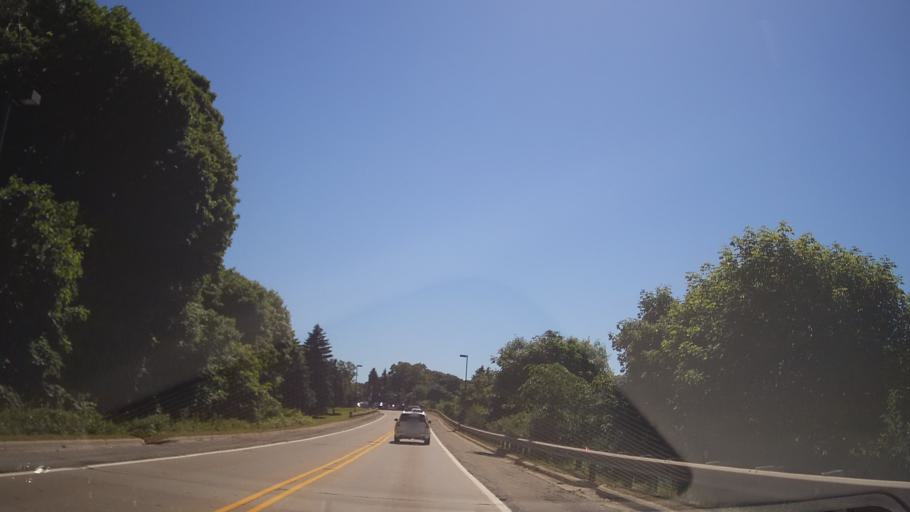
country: US
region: Michigan
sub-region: Emmet County
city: Petoskey
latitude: 45.3766
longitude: -84.9562
